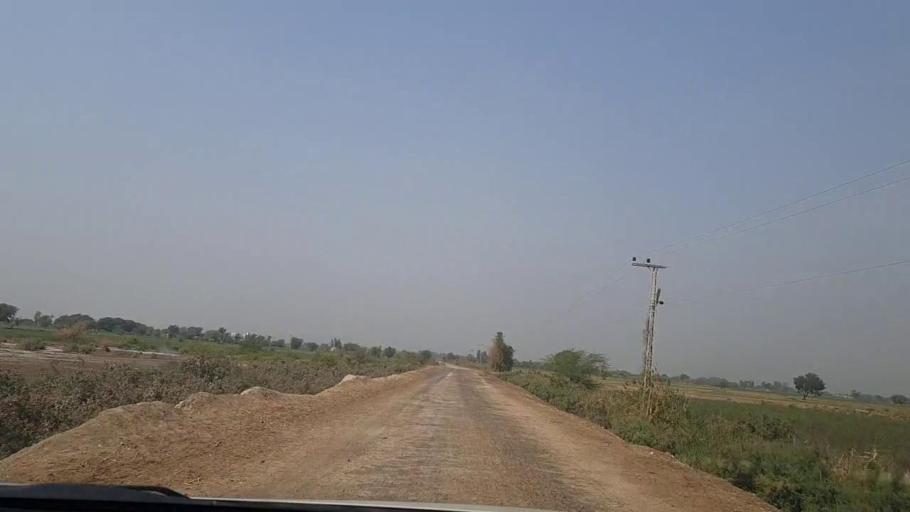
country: PK
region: Sindh
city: Pithoro
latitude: 25.5731
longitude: 69.2038
